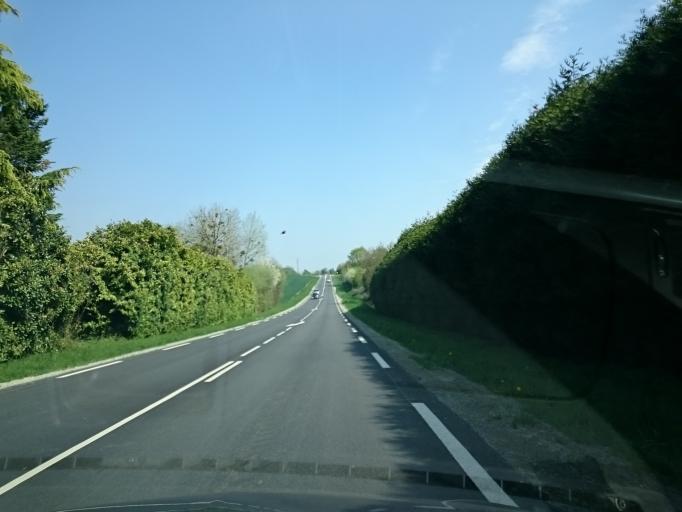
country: FR
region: Brittany
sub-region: Departement d'Ille-et-Vilaine
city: Vern-sur-Seiche
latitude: 48.0486
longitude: -1.5936
